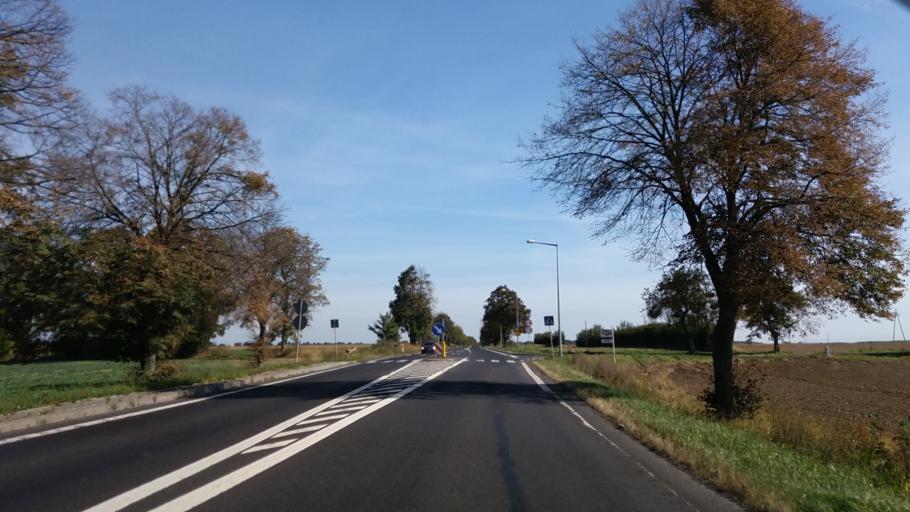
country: PL
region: Greater Poland Voivodeship
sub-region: Powiat miedzychodzki
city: Kwilcz
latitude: 52.5644
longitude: 16.0294
